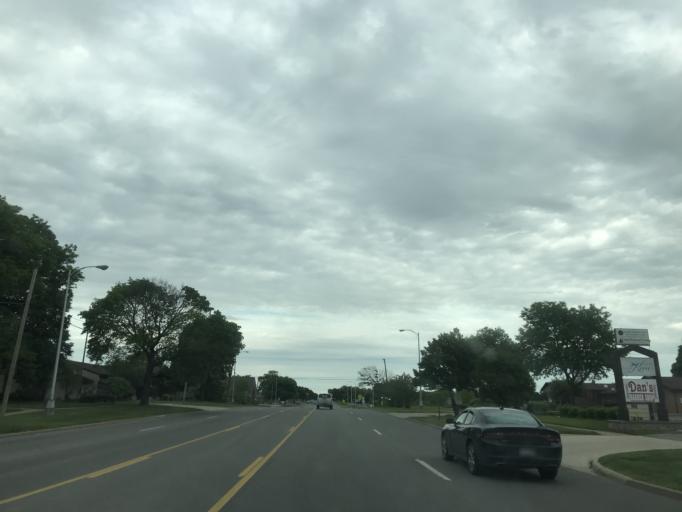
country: US
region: Michigan
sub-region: Wayne County
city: Trenton
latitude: 42.1410
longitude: -83.2084
